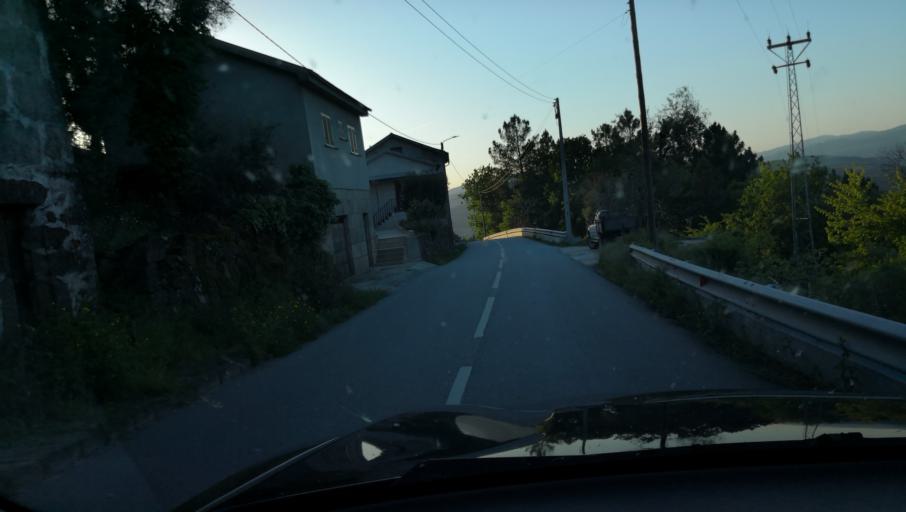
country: PT
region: Vila Real
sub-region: Mondim de Basto
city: Mondim de Basto
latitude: 41.4108
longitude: -7.9331
